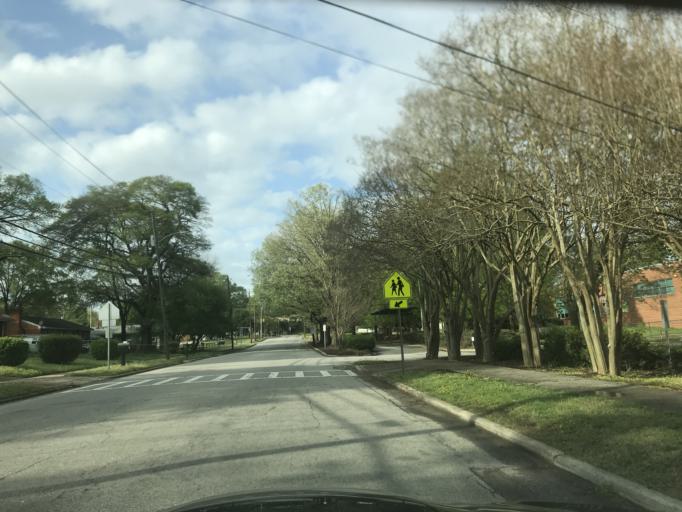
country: US
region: North Carolina
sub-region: Wake County
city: Raleigh
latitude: 35.7732
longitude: -78.6068
